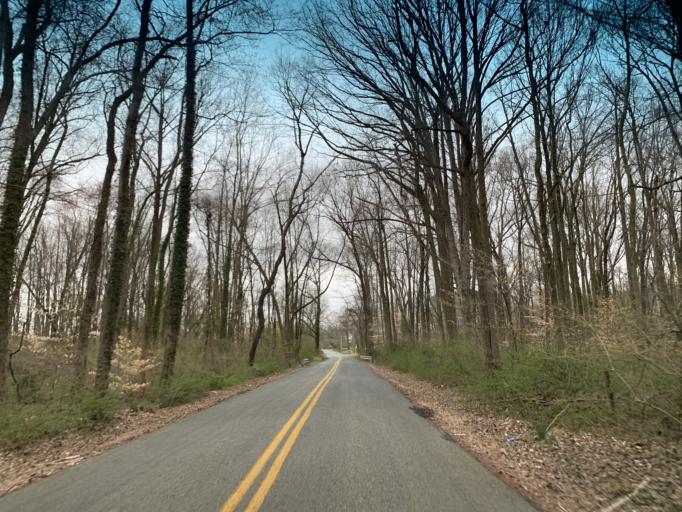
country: US
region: Maryland
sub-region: Harford County
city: Aberdeen
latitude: 39.5690
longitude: -76.1944
